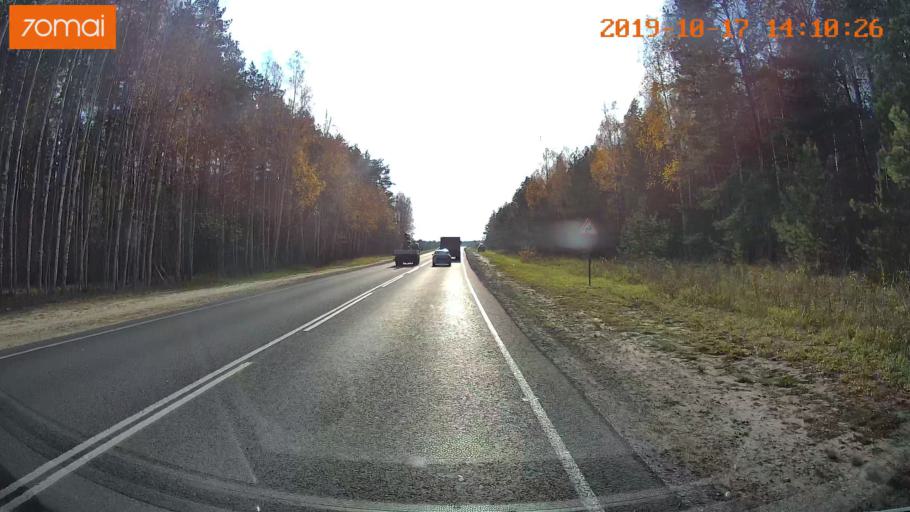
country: RU
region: Rjazan
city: Spas-Klepiki
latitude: 55.0792
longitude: 40.0507
